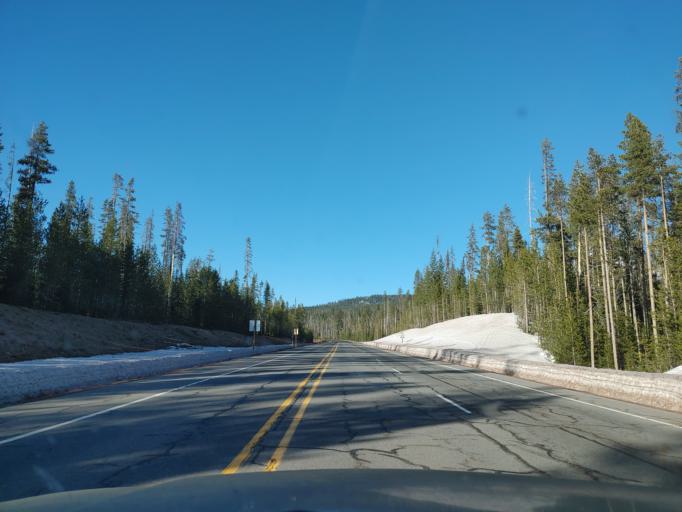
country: US
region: Oregon
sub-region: Lane County
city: Oakridge
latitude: 43.1290
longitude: -122.1300
